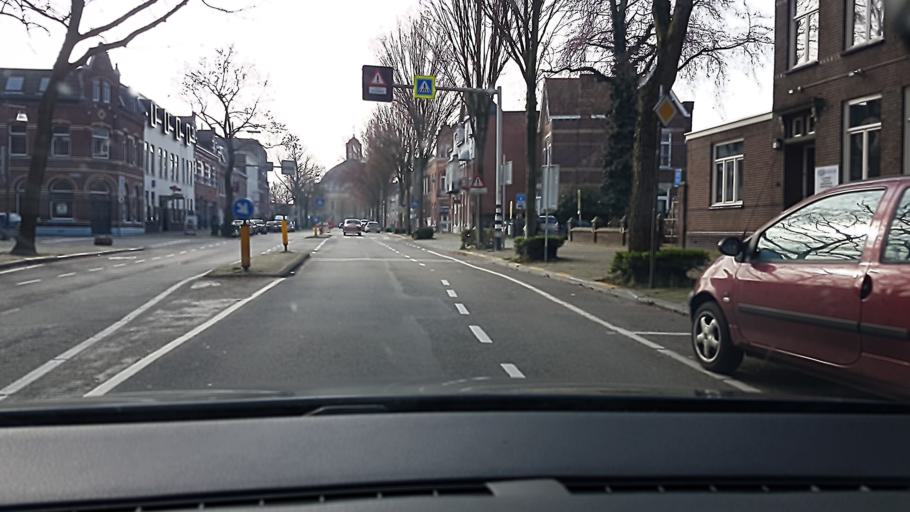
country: NL
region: Limburg
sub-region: Gemeente Roermond
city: Roermond
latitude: 51.1915
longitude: 5.9854
